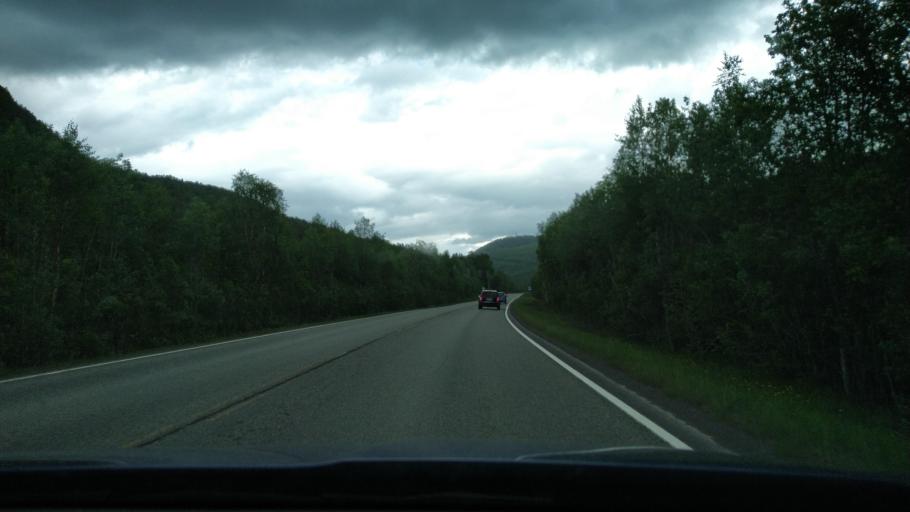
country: NO
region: Troms
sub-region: Malselv
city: Moen
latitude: 68.9771
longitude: 18.5008
